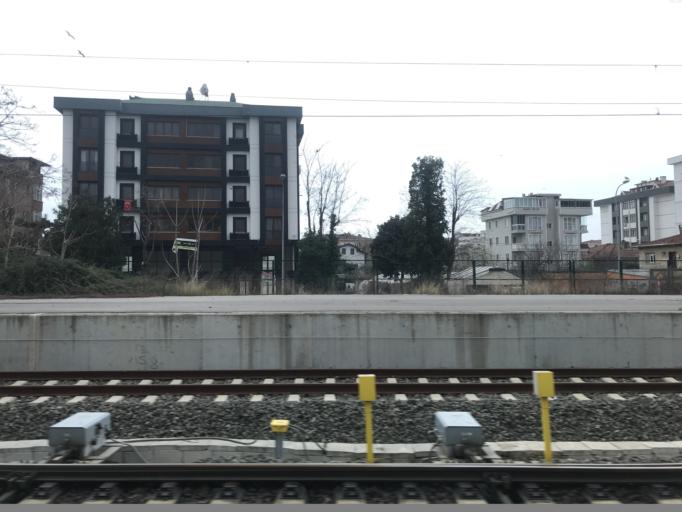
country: TR
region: Istanbul
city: Icmeler
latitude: 40.8288
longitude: 29.3238
